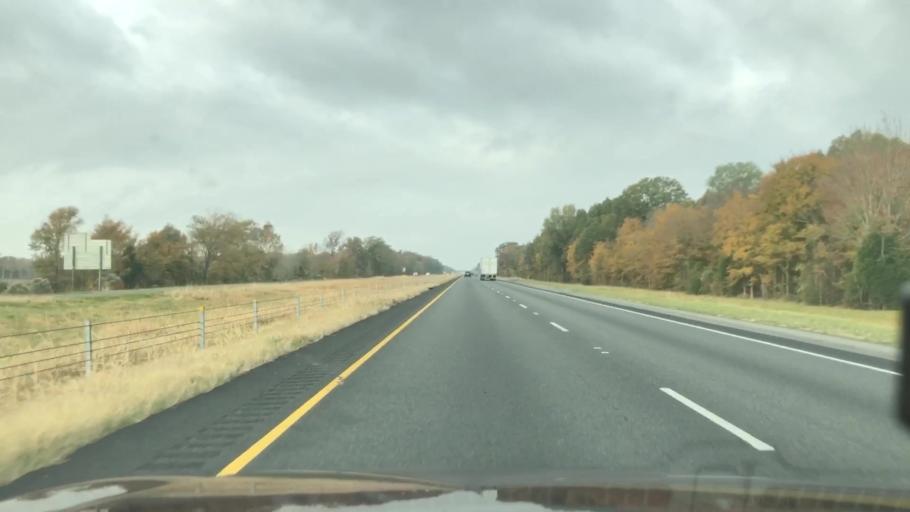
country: US
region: Louisiana
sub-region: Richland Parish
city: Rayville
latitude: 32.4562
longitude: -91.6475
